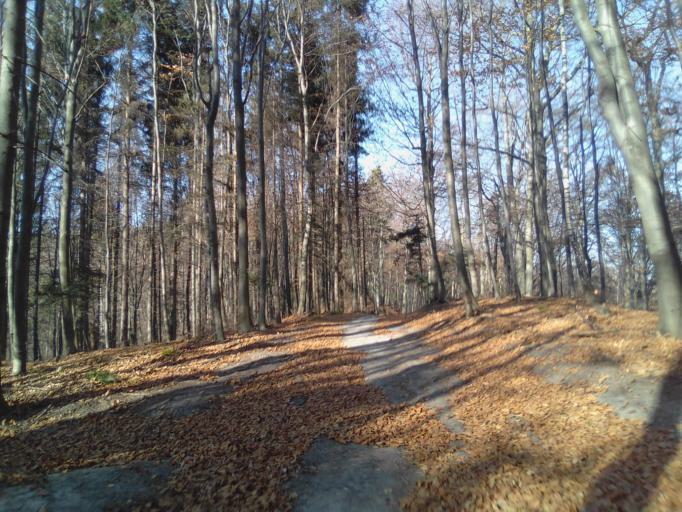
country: PL
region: Subcarpathian Voivodeship
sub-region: Powiat strzyzowski
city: Wysoka Strzyzowska
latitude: 49.8186
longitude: 21.7034
